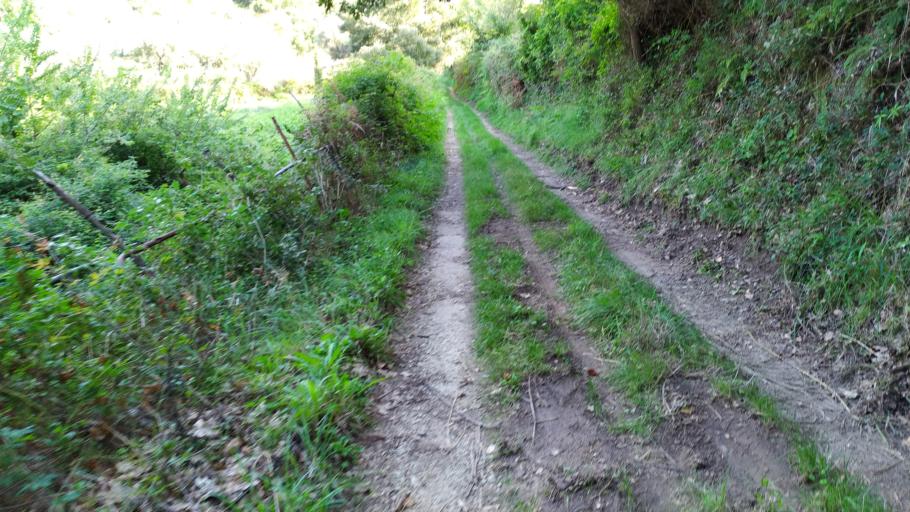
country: IT
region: Sicily
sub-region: Messina
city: Condro
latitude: 38.1618
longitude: 15.3331
